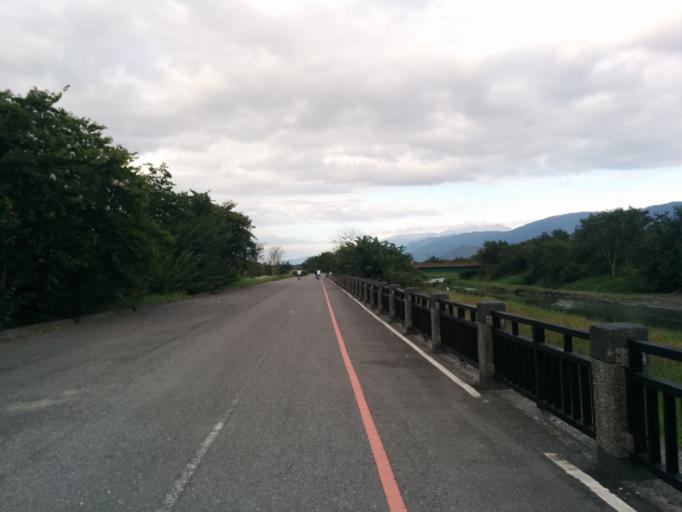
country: TW
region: Taiwan
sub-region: Taitung
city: Taitung
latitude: 23.0250
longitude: 121.1617
